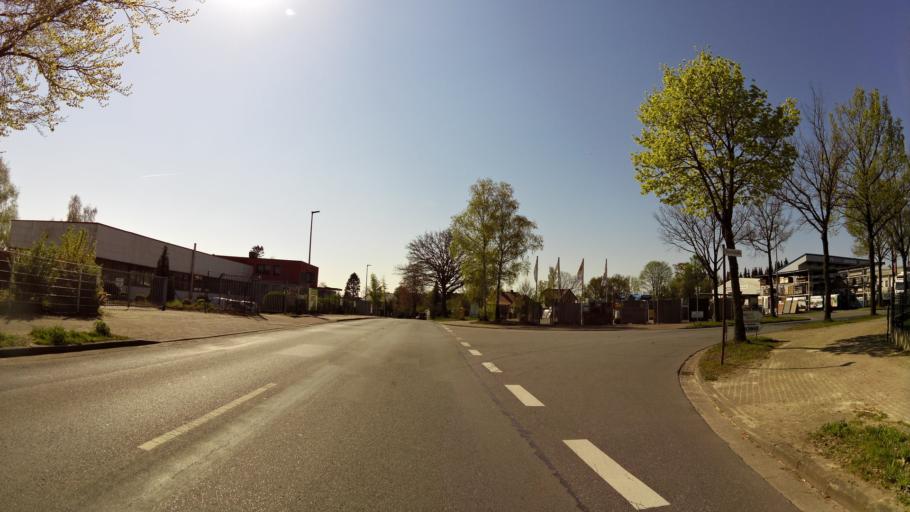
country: DE
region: Lower Saxony
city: Syke
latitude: 52.9161
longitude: 8.8018
